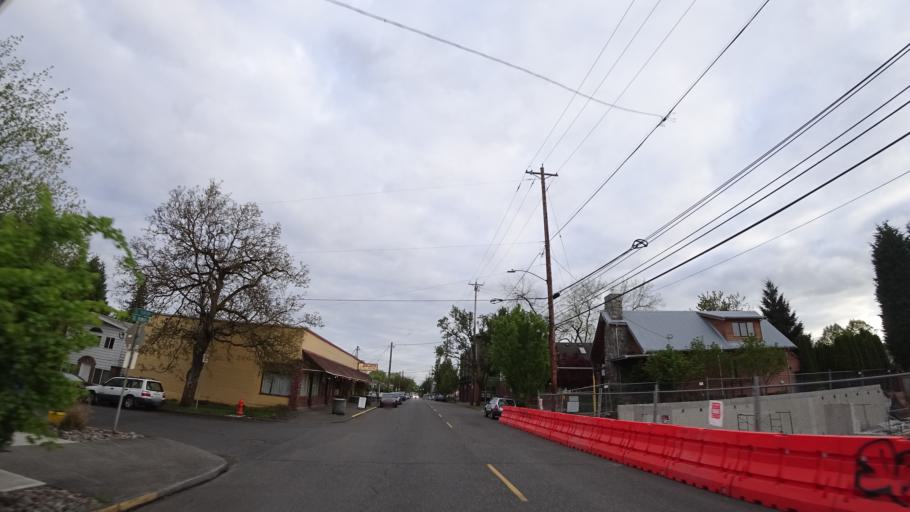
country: US
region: Oregon
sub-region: Clackamas County
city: Milwaukie
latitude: 45.4791
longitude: -122.6494
